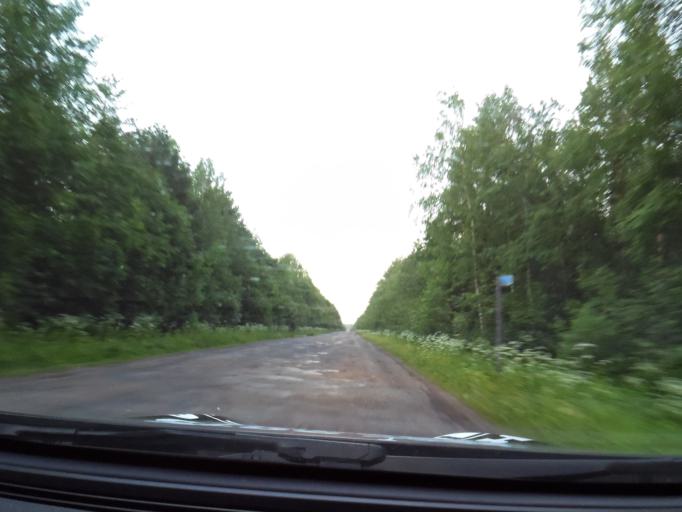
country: RU
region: Leningrad
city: Voznesen'ye
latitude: 60.8297
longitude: 35.6986
